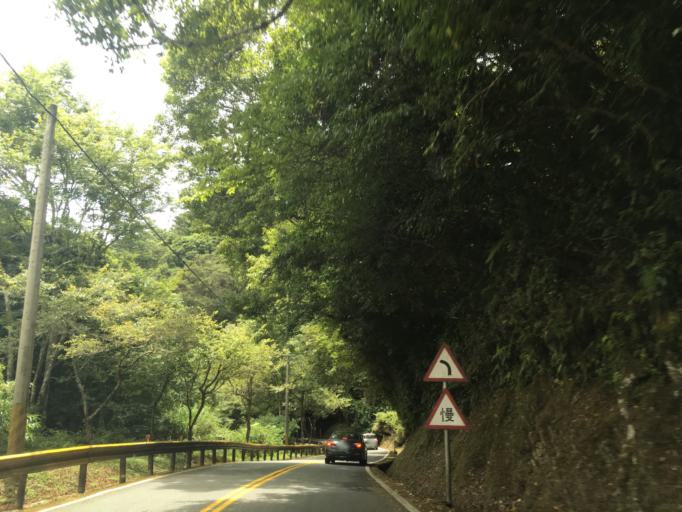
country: TW
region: Taiwan
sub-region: Hualien
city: Hualian
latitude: 24.1812
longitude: 121.3983
